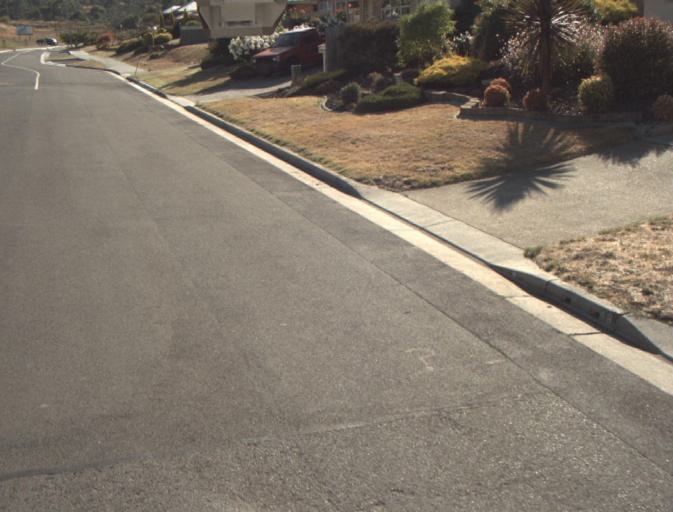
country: AU
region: Tasmania
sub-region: Launceston
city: Newnham
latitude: -41.3945
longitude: 147.1332
